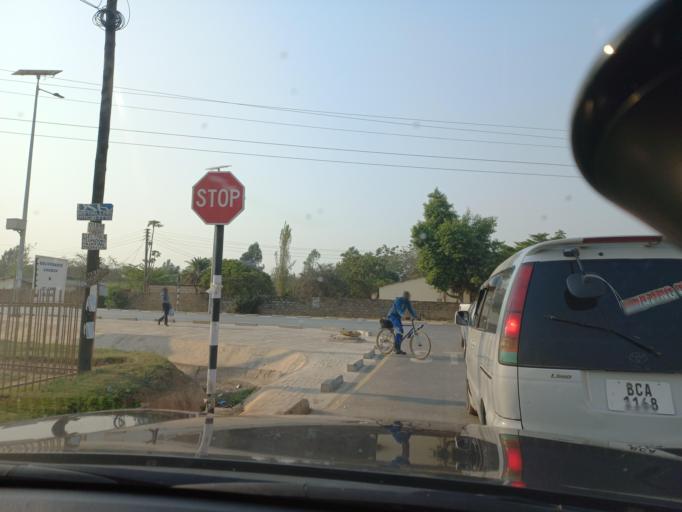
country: ZM
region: Lusaka
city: Lusaka
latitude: -15.4082
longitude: 28.3459
